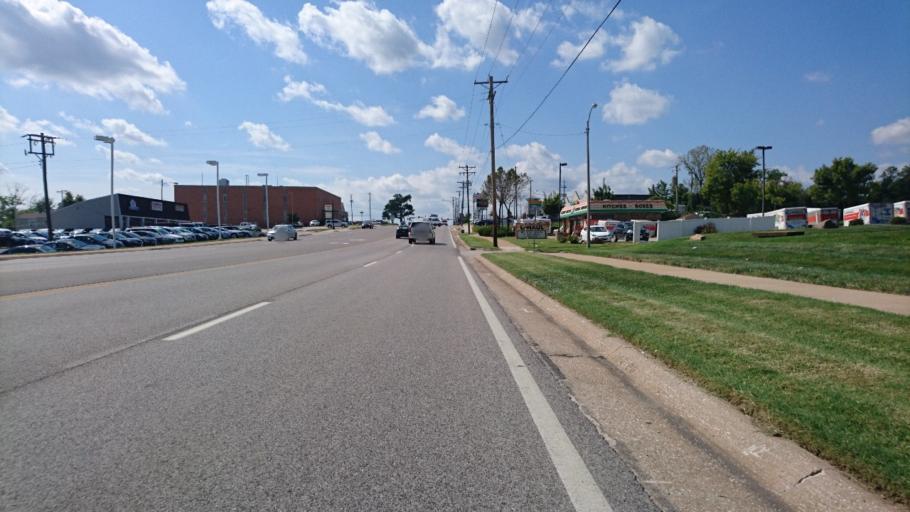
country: US
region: Missouri
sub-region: Saint Louis County
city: Winchester
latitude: 38.5931
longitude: -90.5339
